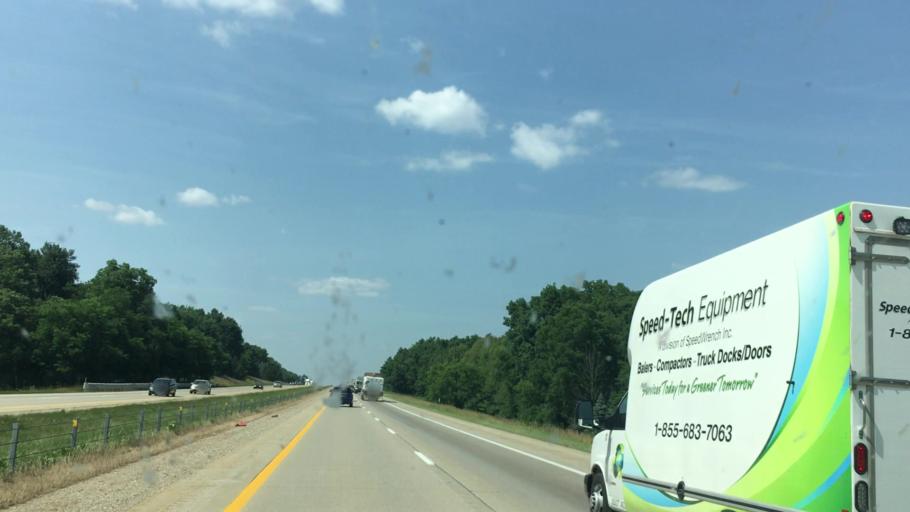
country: US
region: Michigan
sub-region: Allegan County
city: Otsego
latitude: 42.4993
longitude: -85.6526
